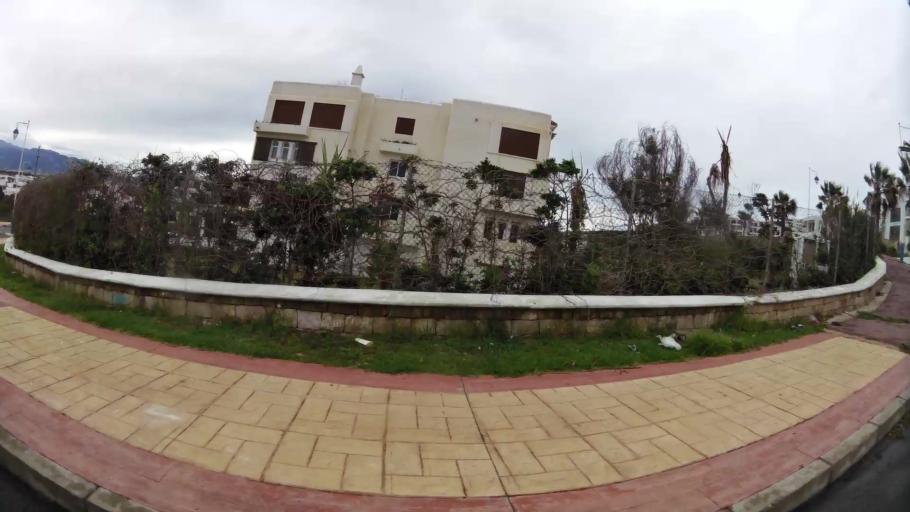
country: MA
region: Tanger-Tetouan
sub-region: Tetouan
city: Martil
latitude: 35.6652
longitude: -5.2897
